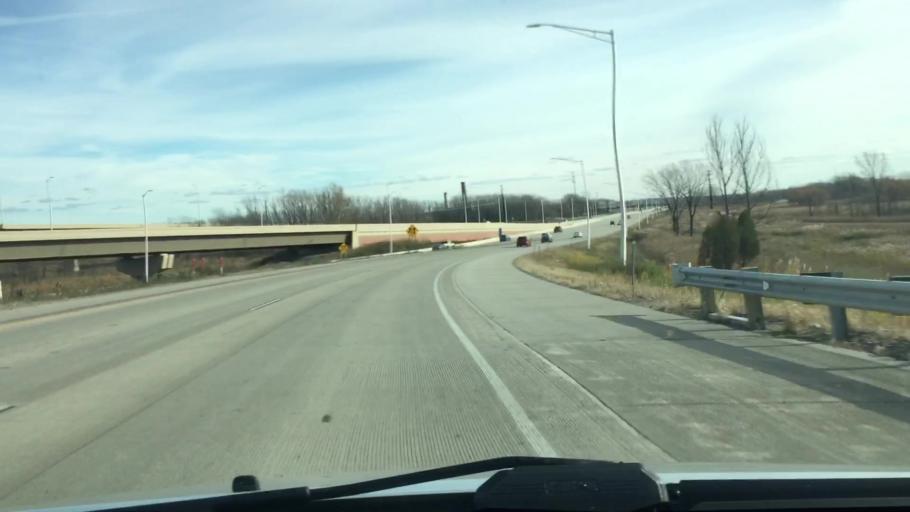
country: US
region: Wisconsin
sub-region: Brown County
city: Howard
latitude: 44.5584
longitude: -88.0512
